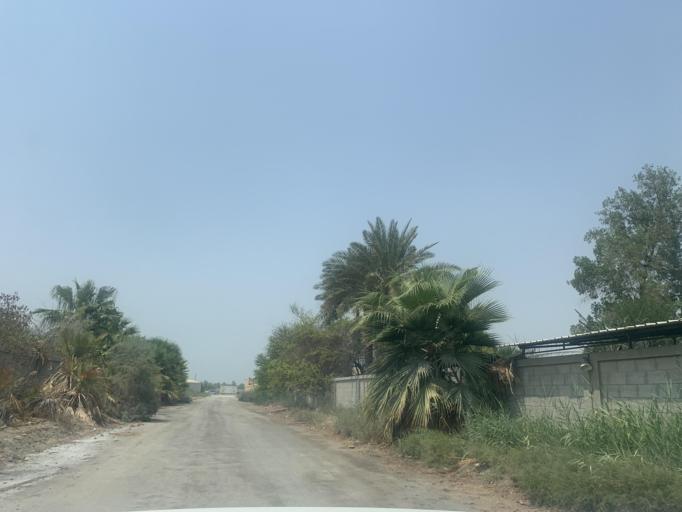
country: BH
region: Central Governorate
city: Madinat Hamad
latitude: 26.1236
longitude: 50.4662
